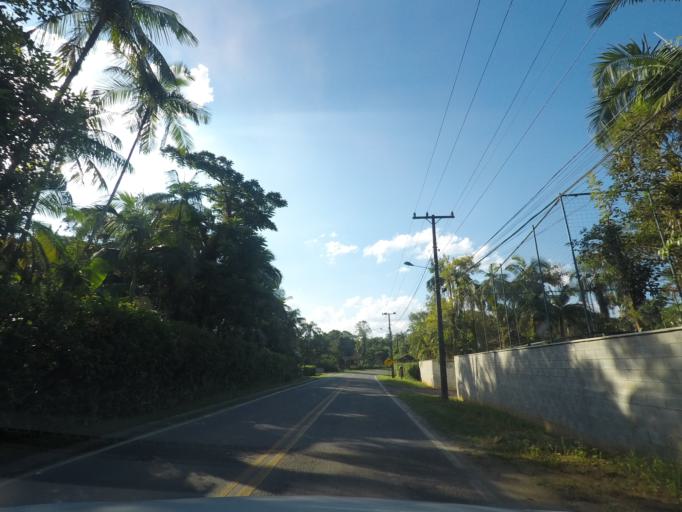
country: BR
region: Parana
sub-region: Antonina
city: Antonina
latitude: -25.4356
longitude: -48.8761
